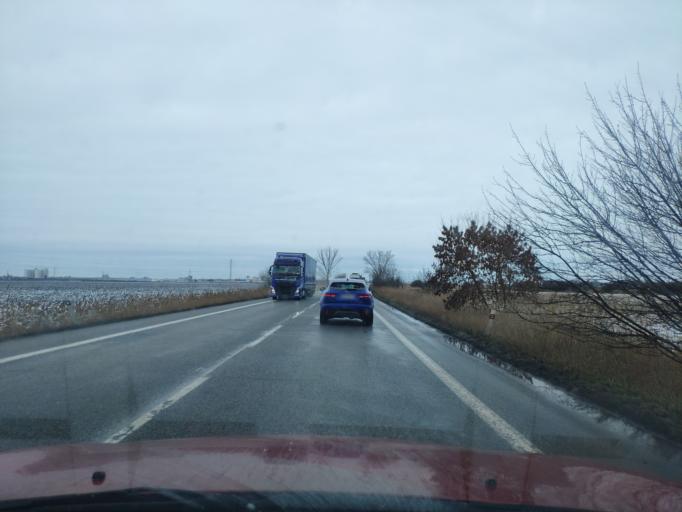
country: SK
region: Trnavsky
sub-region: Okres Galanta
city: Galanta
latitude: 48.1833
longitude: 17.7680
